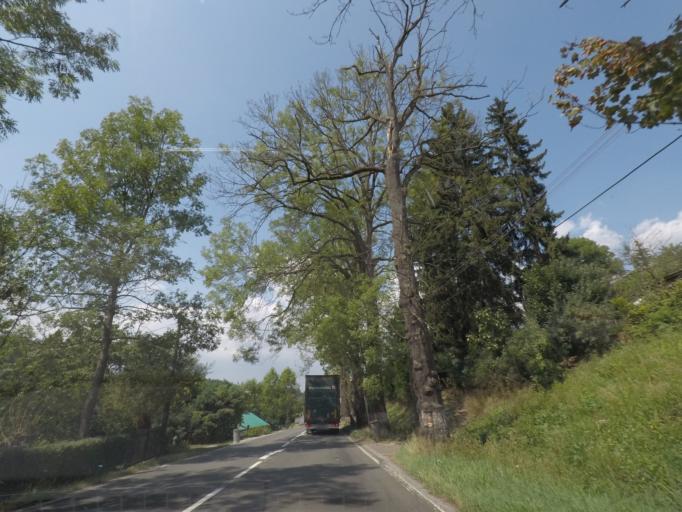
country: CZ
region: Kralovehradecky
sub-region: Okres Trutnov
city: Hostinne
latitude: 50.5164
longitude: 15.7358
